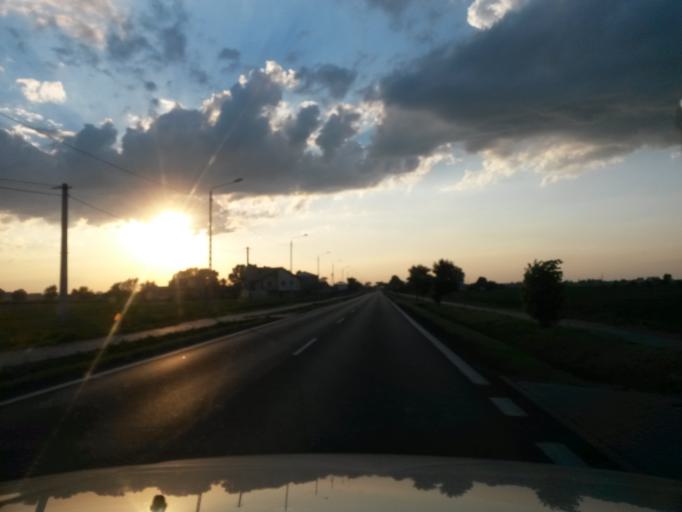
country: PL
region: Lodz Voivodeship
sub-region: Powiat wielunski
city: Wielun
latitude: 51.2403
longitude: 18.5292
